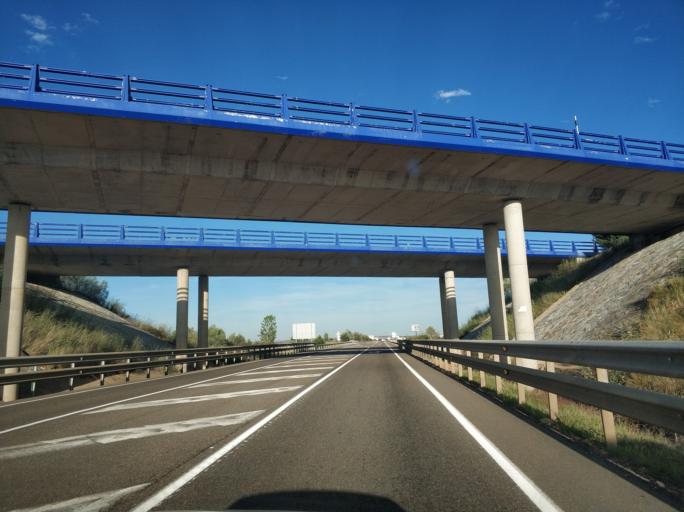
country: ES
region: Castille and Leon
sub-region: Provincia de Leon
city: Villamanan
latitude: 42.3261
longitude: -5.6094
